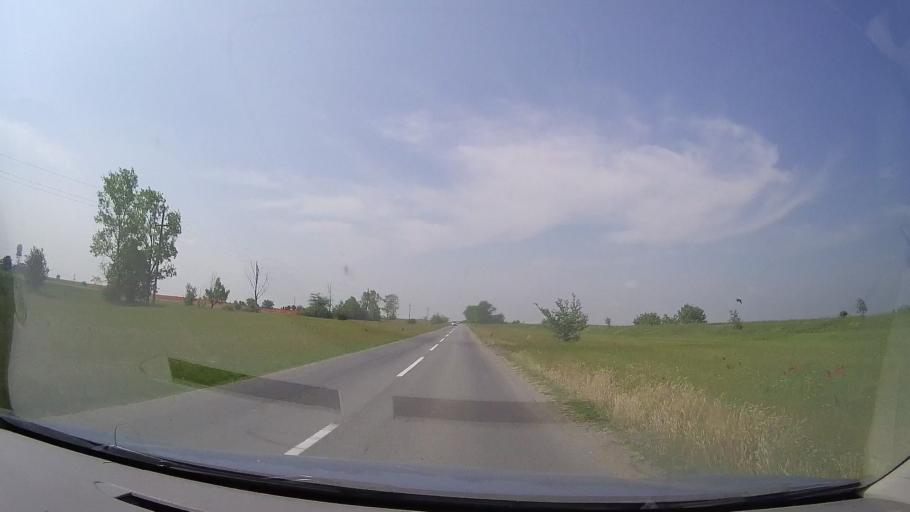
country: RS
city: Samos
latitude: 45.1917
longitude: 20.7673
